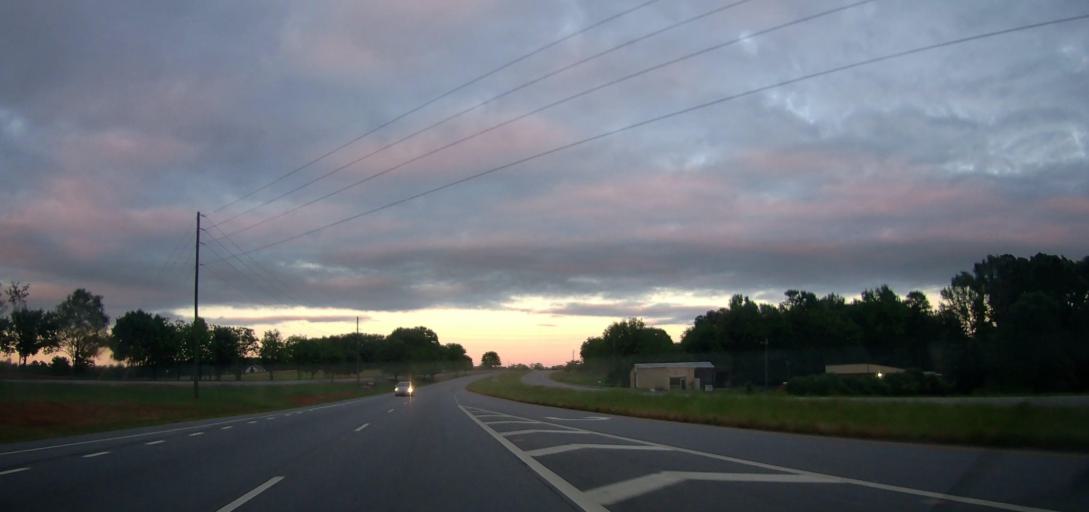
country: US
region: Georgia
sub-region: Clarke County
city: Country Club Estates
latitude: 34.0091
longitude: -83.4694
